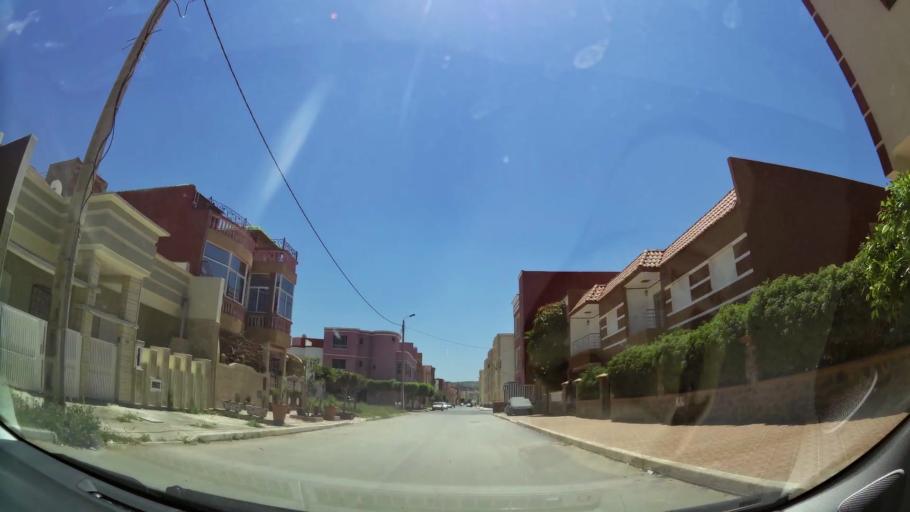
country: MA
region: Oriental
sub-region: Berkane-Taourirt
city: Madagh
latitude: 35.0823
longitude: -2.2361
